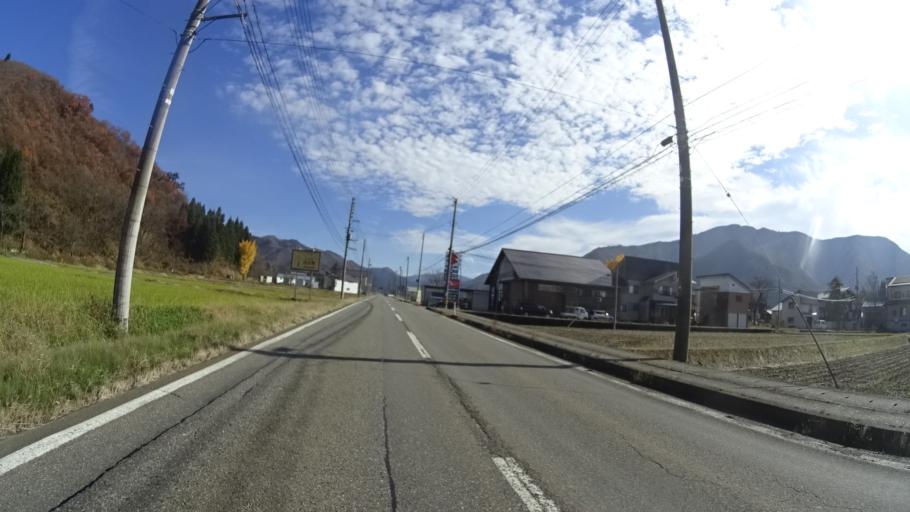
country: JP
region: Niigata
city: Muikamachi
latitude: 37.2282
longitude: 138.9892
